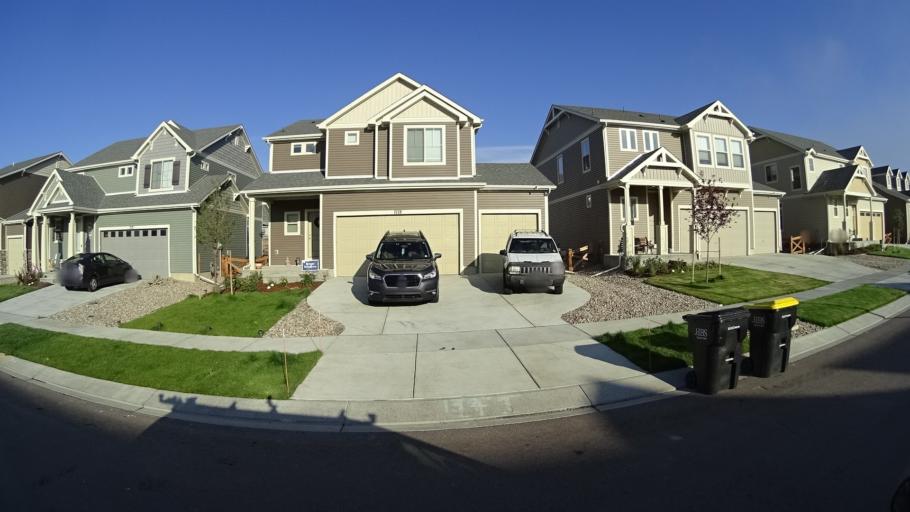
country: US
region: Colorado
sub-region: El Paso County
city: Cimarron Hills
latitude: 38.9336
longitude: -104.6562
